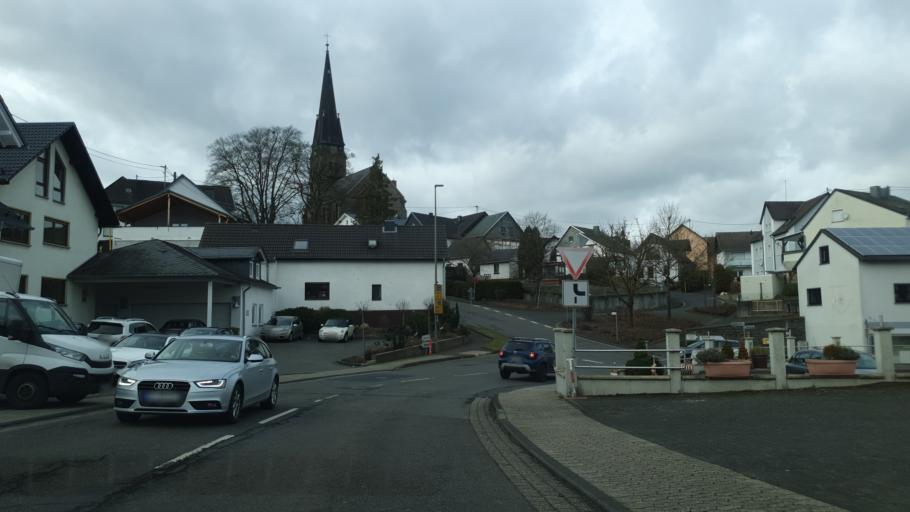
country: DE
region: Rheinland-Pfalz
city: Puderbach
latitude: 50.5958
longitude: 7.6093
